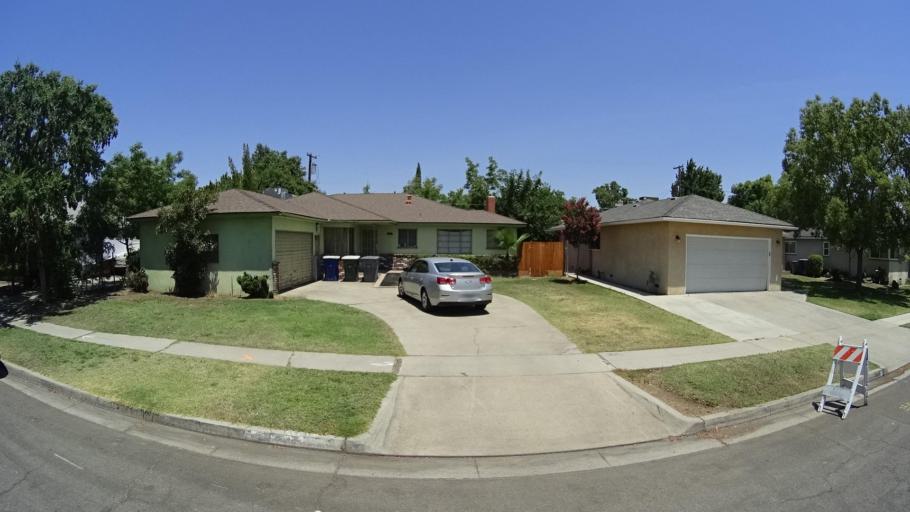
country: US
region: California
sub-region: Fresno County
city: Fresno
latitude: 36.7958
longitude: -119.7696
